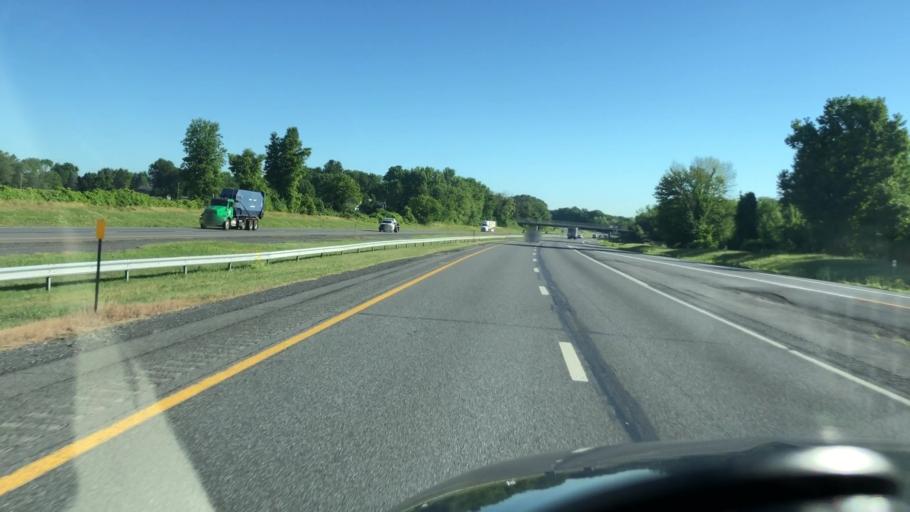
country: US
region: New York
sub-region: Rensselaer County
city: Castleton-on-Hudson
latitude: 42.5360
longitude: -73.7834
